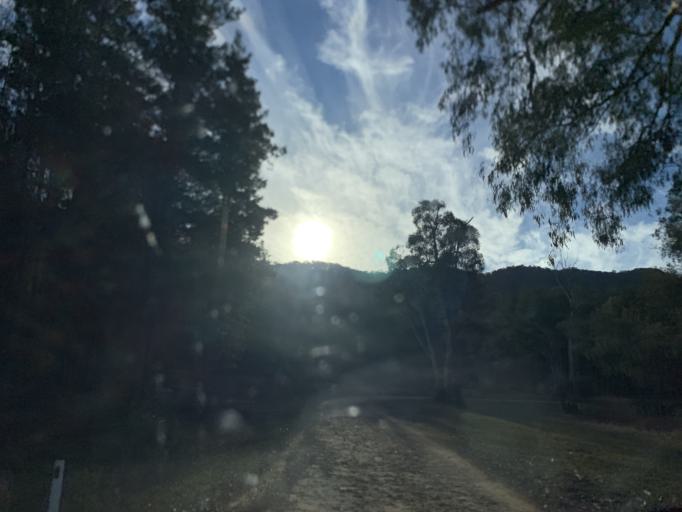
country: AU
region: Victoria
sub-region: Mansfield
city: Mansfield
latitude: -36.9337
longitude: 146.0929
